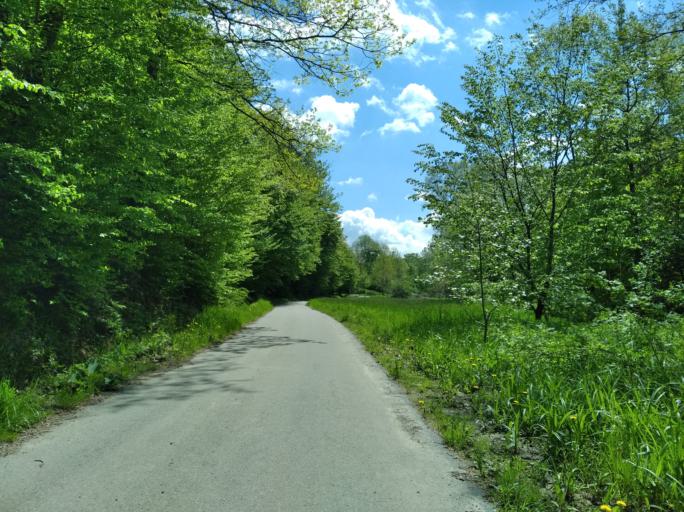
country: PL
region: Subcarpathian Voivodeship
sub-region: Powiat strzyzowski
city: Wisniowa
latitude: 49.8428
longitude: 21.6414
